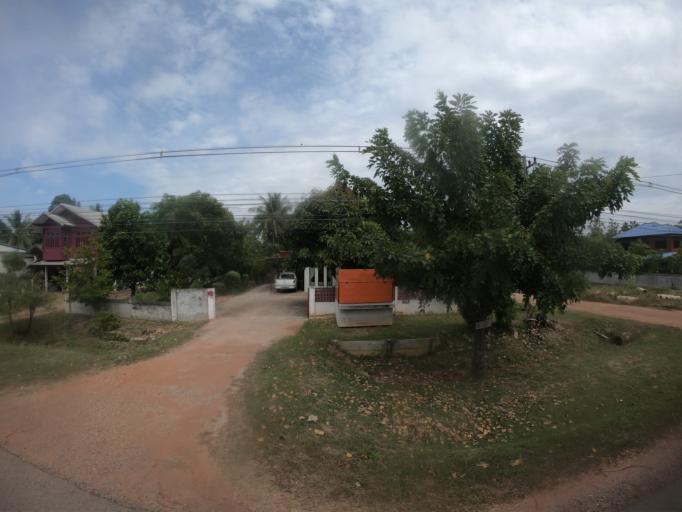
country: TH
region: Maha Sarakham
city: Chiang Yuen
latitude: 16.3445
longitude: 103.1276
